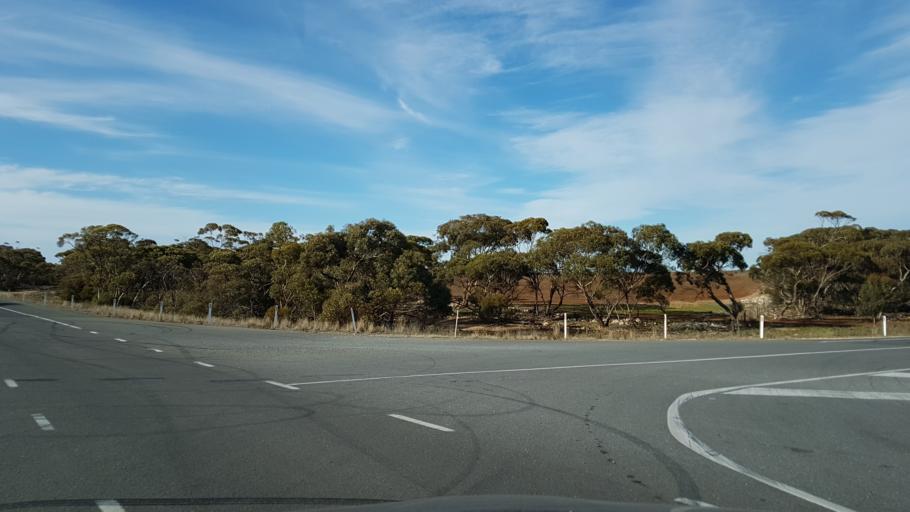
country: AU
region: South Australia
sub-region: Murray Bridge
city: Tailem Bend
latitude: -35.0877
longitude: 139.4657
